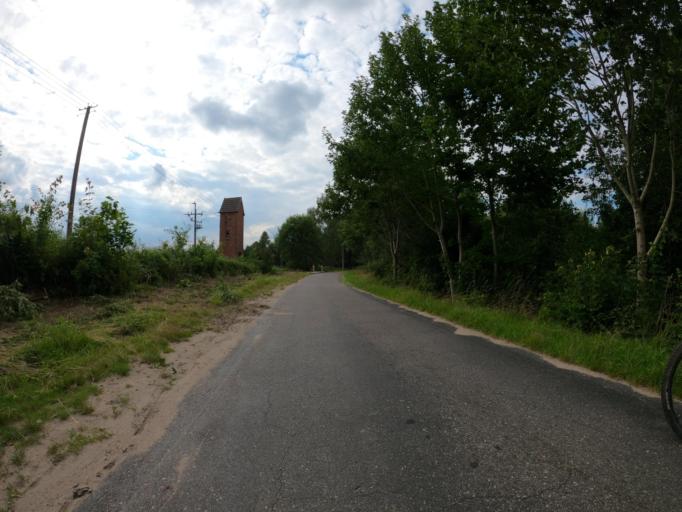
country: PL
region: West Pomeranian Voivodeship
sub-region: Powiat szczecinecki
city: Borne Sulinowo
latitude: 53.6294
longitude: 16.5564
